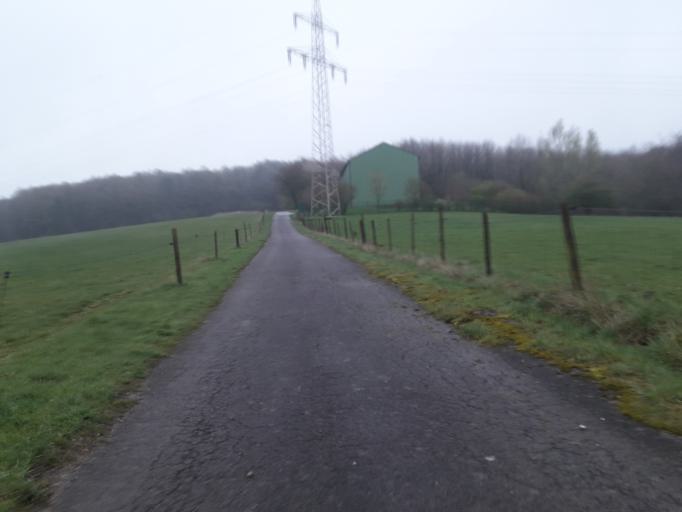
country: DE
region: North Rhine-Westphalia
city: Bad Lippspringe
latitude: 51.7447
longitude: 8.8633
